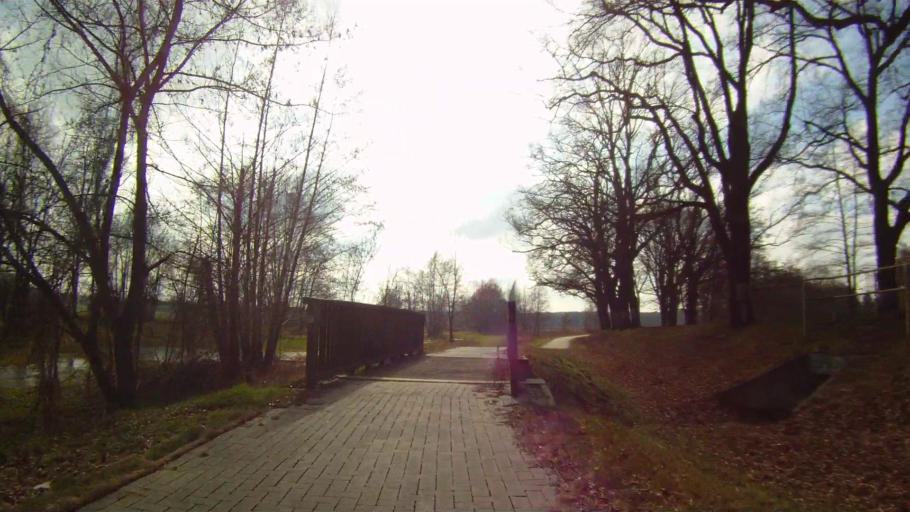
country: DE
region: Brandenburg
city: Erkner
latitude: 52.3965
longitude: 13.7482
